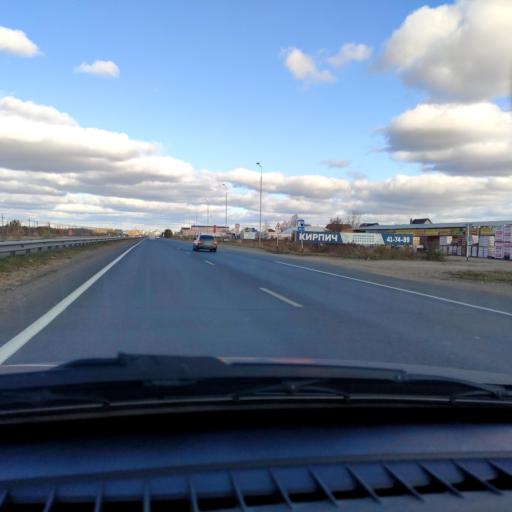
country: RU
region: Samara
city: Tol'yatti
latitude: 53.5688
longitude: 49.3786
